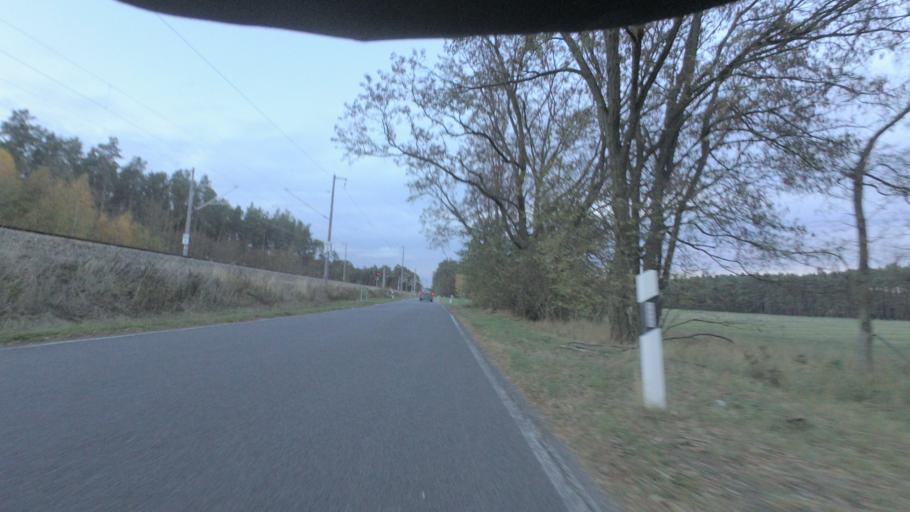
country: DE
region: Brandenburg
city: Sonnewalde
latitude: 51.7613
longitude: 13.6137
